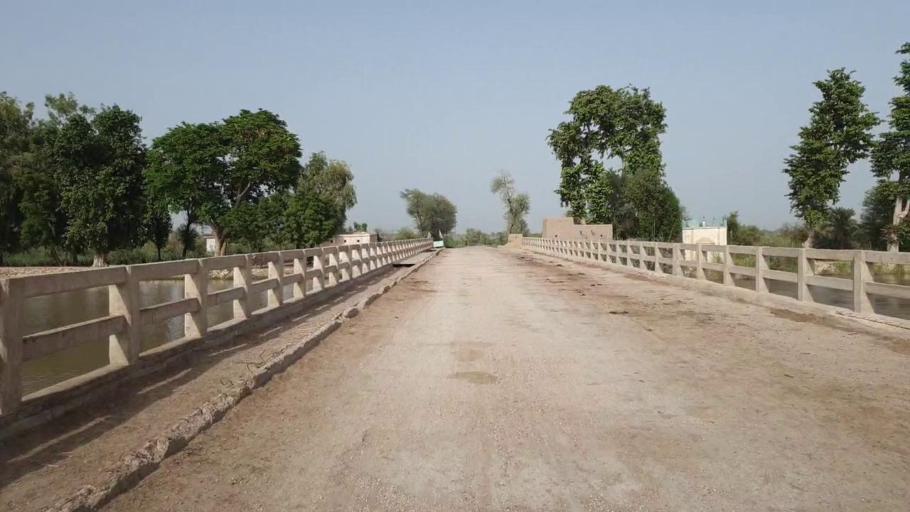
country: PK
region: Sindh
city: Daur
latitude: 26.4570
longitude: 68.1581
